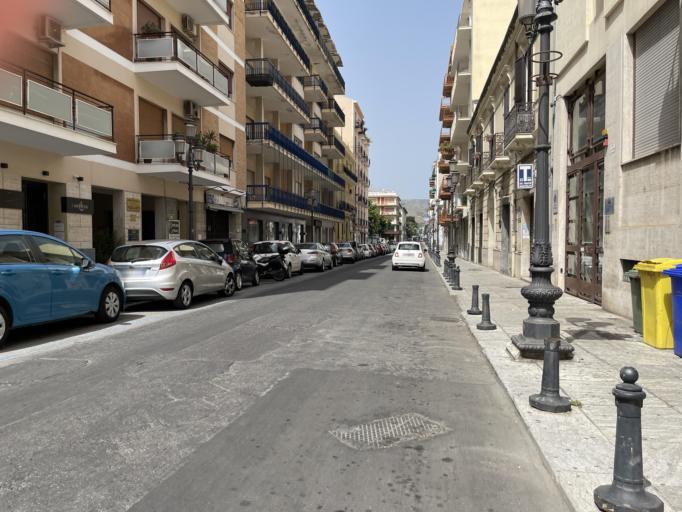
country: IT
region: Calabria
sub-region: Provincia di Reggio Calabria
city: Reggio Calabria
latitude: 38.1019
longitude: 15.6362
